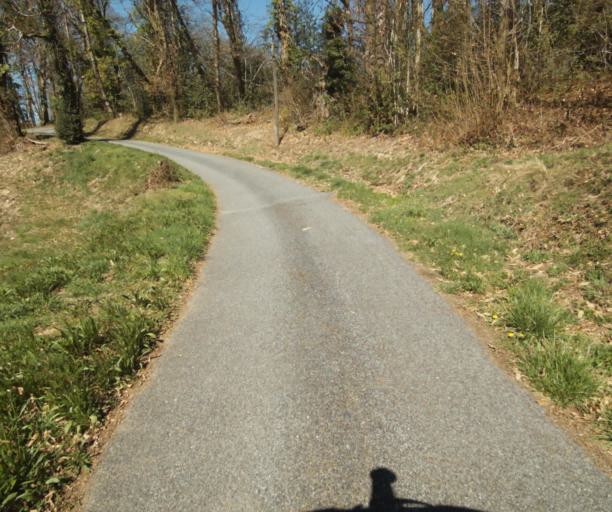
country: FR
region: Limousin
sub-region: Departement de la Correze
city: Saint-Mexant
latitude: 45.2881
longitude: 1.6360
